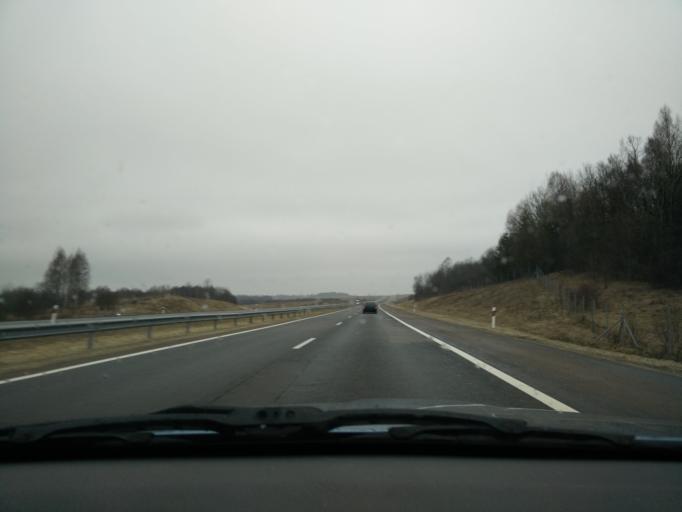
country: LT
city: Silale
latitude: 55.5796
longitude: 22.1565
